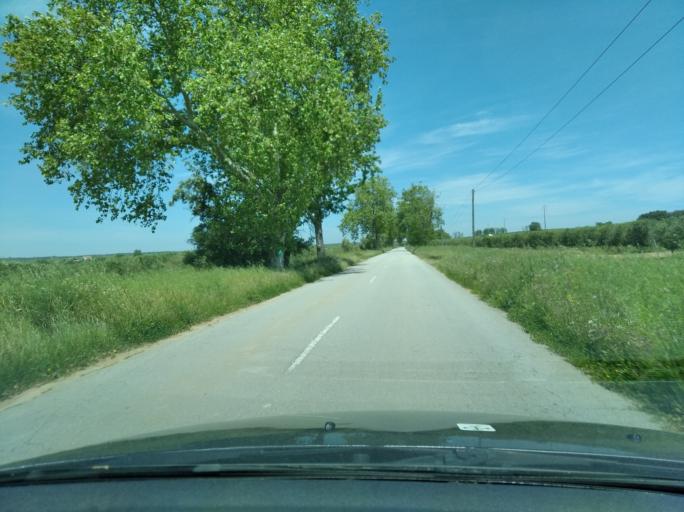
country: PT
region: Portalegre
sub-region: Avis
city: Avis
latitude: 39.0756
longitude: -7.8813
